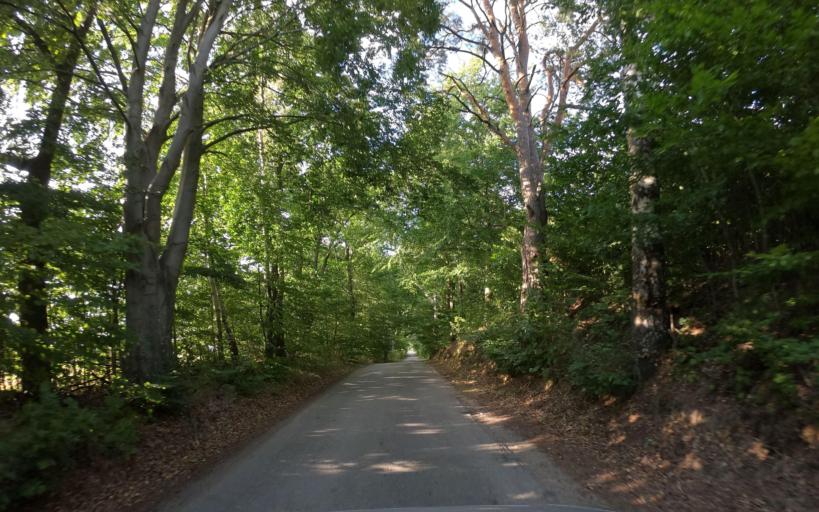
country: PL
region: West Pomeranian Voivodeship
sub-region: Powiat drawski
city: Czaplinek
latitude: 53.5533
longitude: 16.1726
